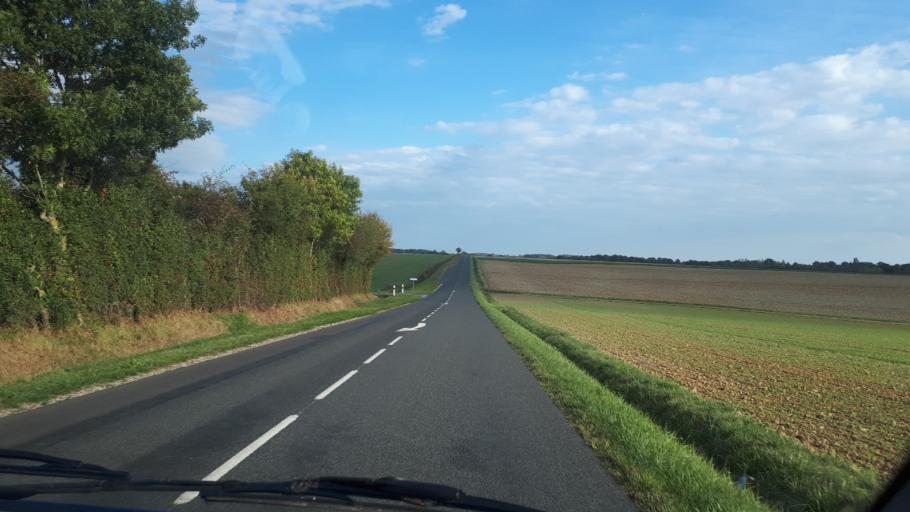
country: FR
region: Centre
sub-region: Departement du Loir-et-Cher
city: Sarge-sur-Braye
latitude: 47.9085
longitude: 0.9306
